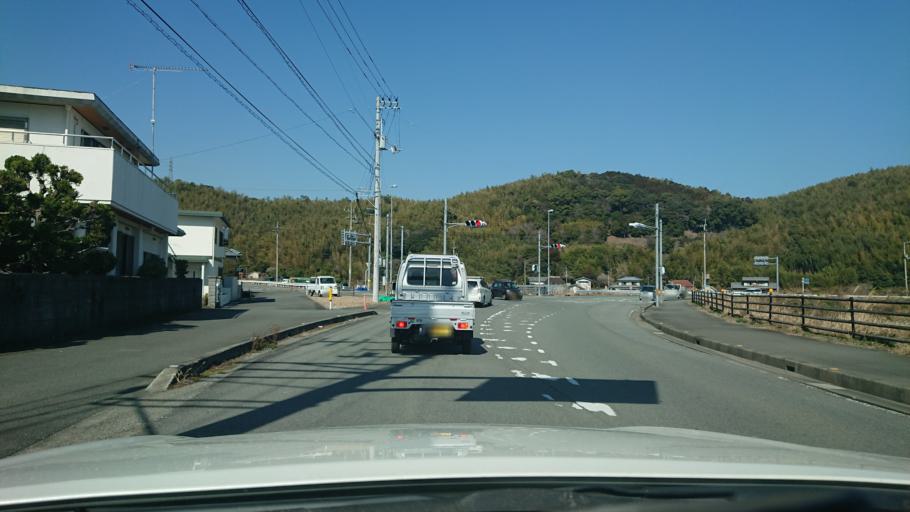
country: JP
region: Tokushima
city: Komatsushimacho
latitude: 33.9699
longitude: 134.5998
